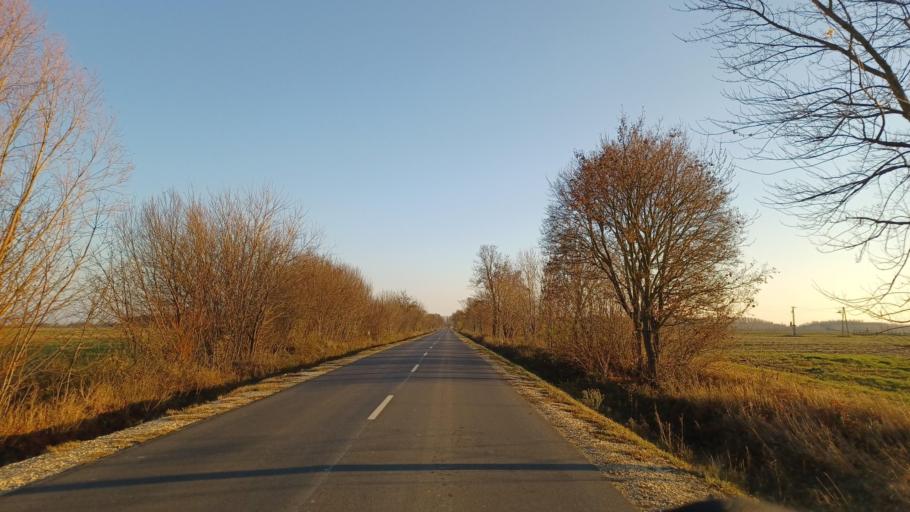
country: HU
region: Tolna
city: Fadd
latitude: 46.4943
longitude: 18.8321
